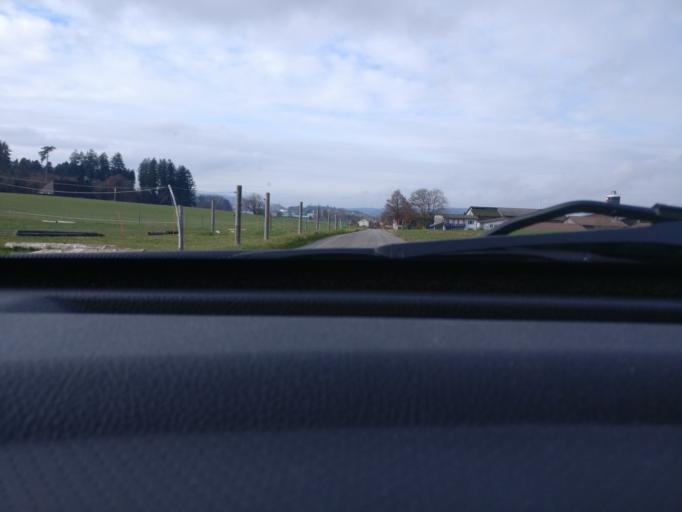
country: CH
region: Bern
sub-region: Bern-Mittelland District
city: Urtenen
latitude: 47.0070
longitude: 7.4904
